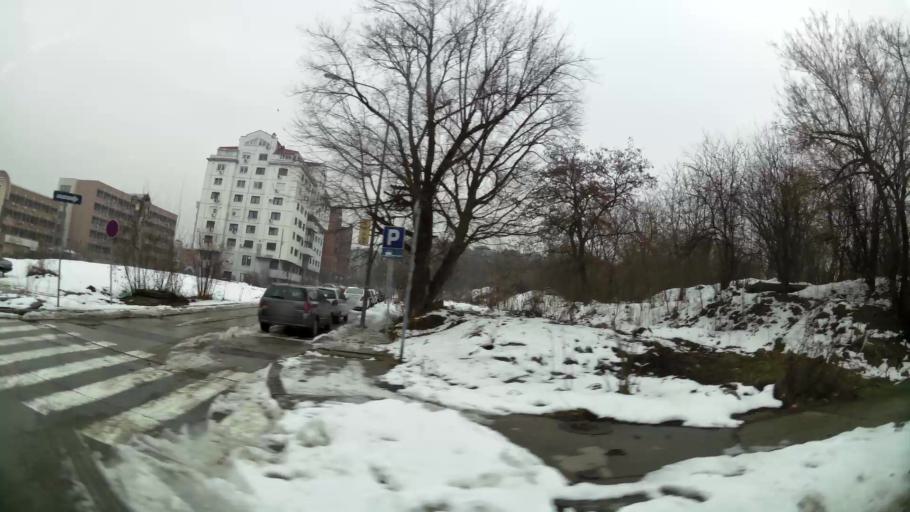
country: RS
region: Central Serbia
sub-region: Belgrade
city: Vozdovac
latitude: 44.7830
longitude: 20.4912
